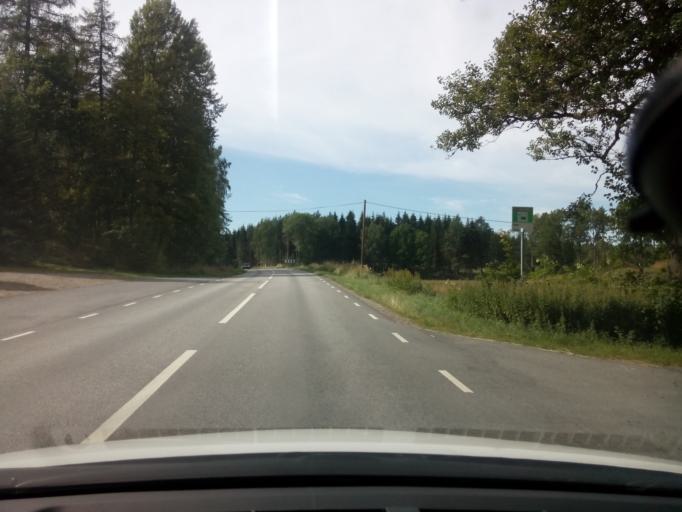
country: SE
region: Soedermanland
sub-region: Oxelosunds Kommun
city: Oxelosund
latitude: 58.7406
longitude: 17.1896
